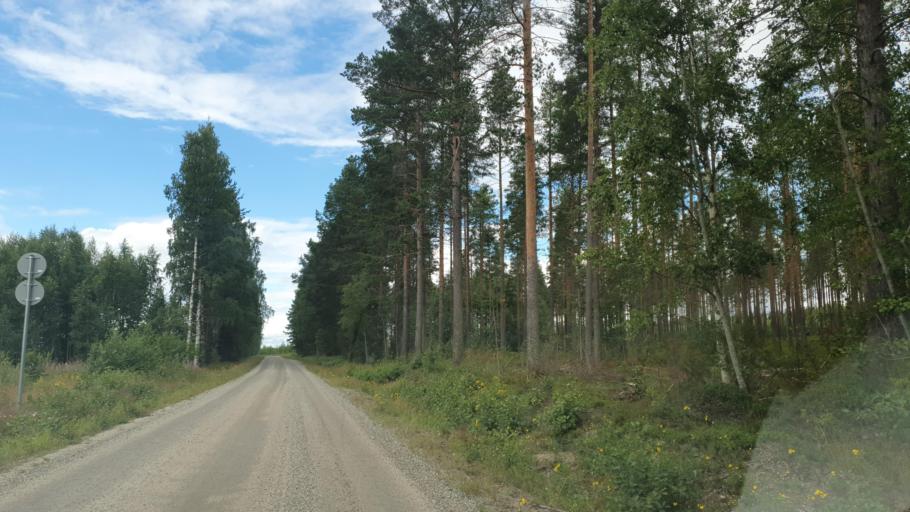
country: FI
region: Kainuu
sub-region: Kehys-Kainuu
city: Kuhmo
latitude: 64.1095
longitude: 29.3824
